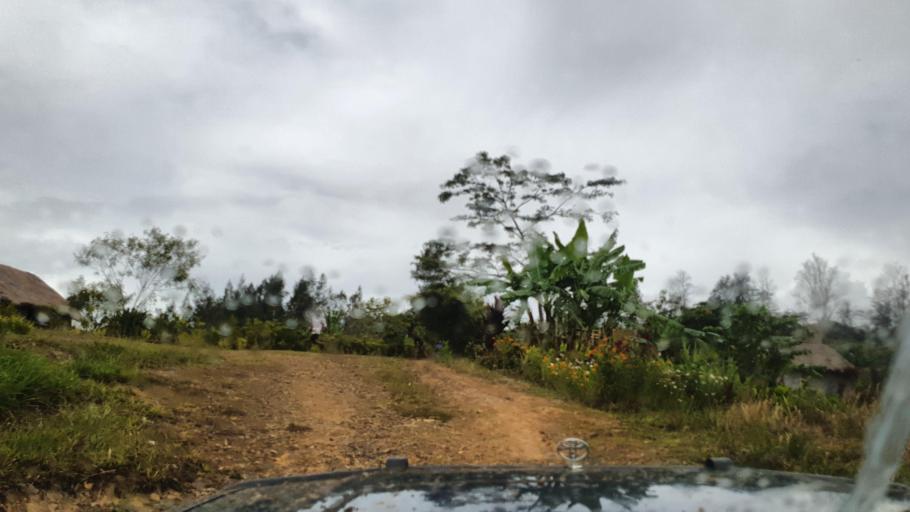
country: PG
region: Jiwaka
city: Minj
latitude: -5.9525
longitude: 144.7774
